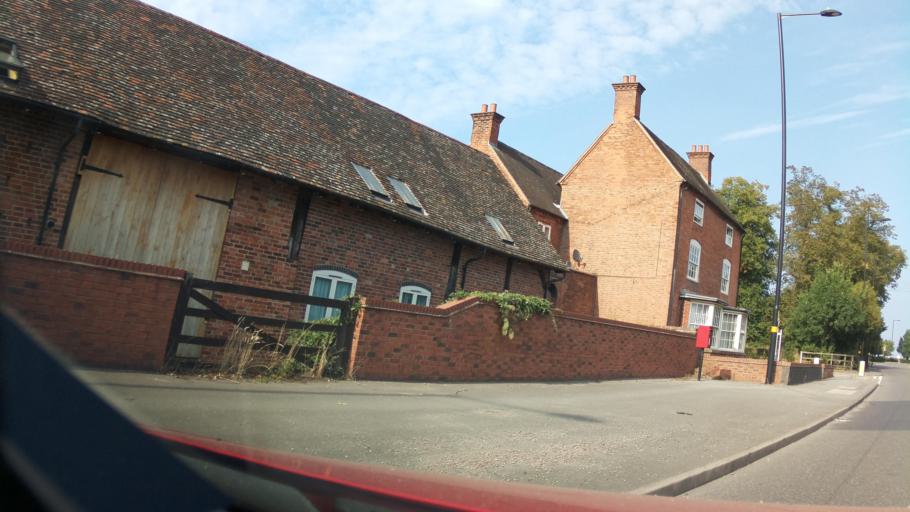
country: GB
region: England
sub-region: Warwickshire
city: Curdworth
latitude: 52.5304
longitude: -1.7559
